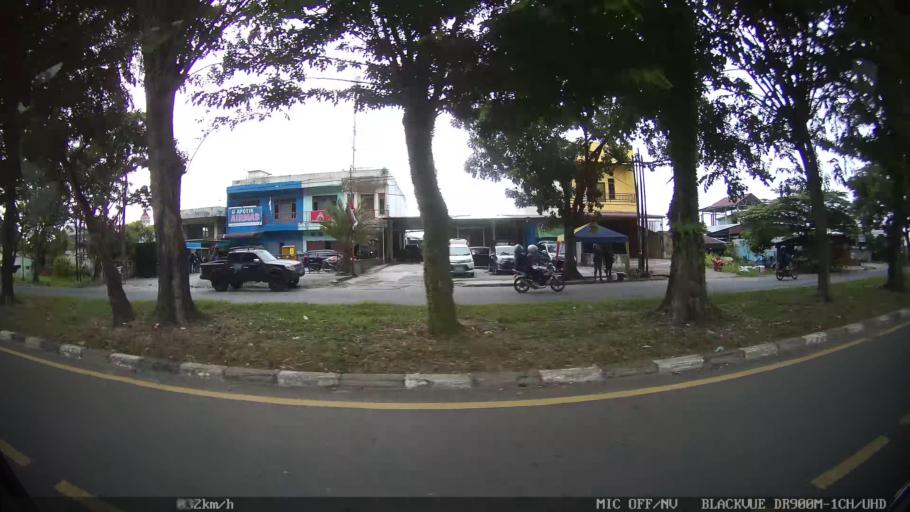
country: ID
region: North Sumatra
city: Medan
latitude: 3.5405
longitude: 98.6479
